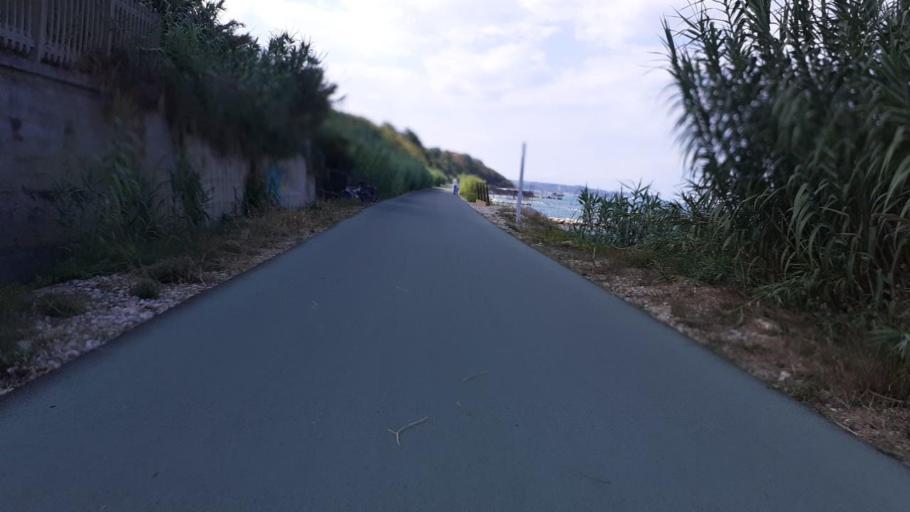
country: IT
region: Abruzzo
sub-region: Provincia di Chieti
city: Marina di San Vito
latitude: 42.2879
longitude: 14.4795
